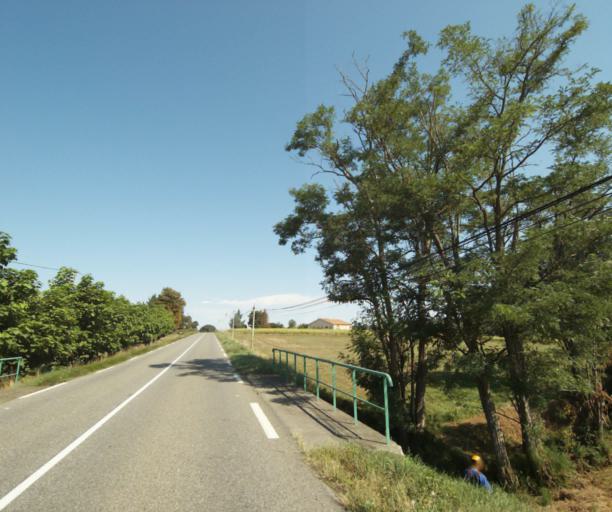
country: FR
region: Midi-Pyrenees
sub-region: Departement de l'Ariege
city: Lezat-sur-Leze
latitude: 43.2921
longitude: 1.3421
